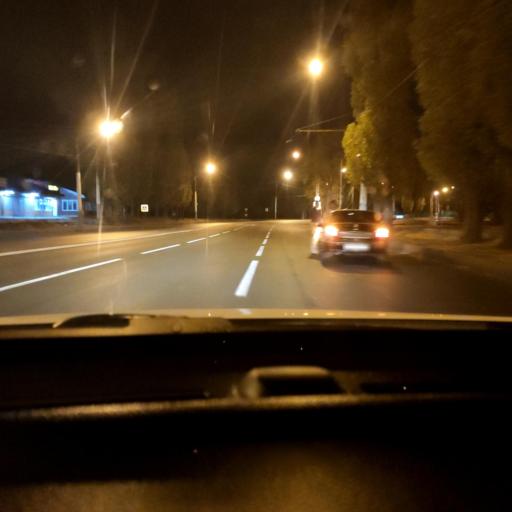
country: RU
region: Voronezj
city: Maslovka
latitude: 51.6015
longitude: 39.2392
